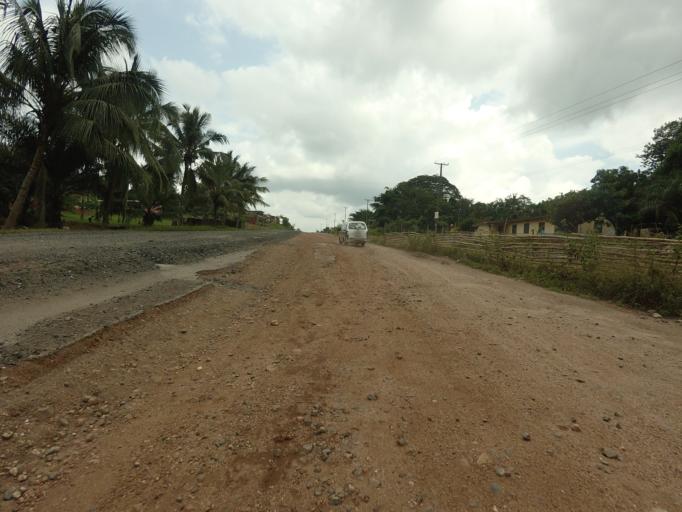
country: GH
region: Volta
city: Ho
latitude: 6.6258
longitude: 0.3109
